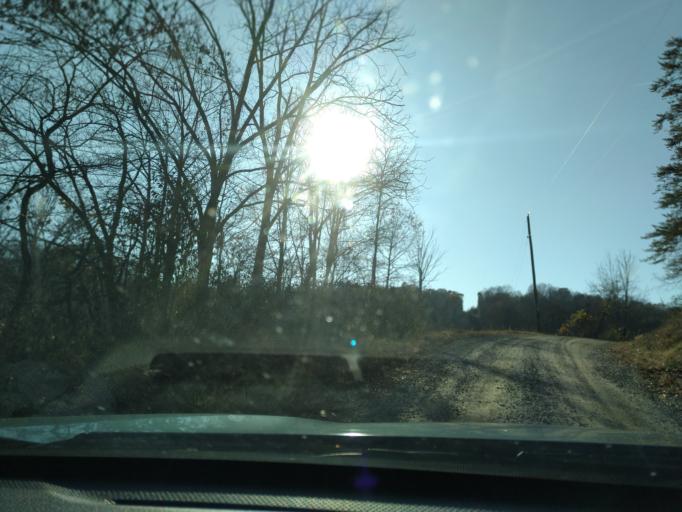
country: US
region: Virginia
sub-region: Floyd County
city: Floyd
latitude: 36.8376
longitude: -80.1865
